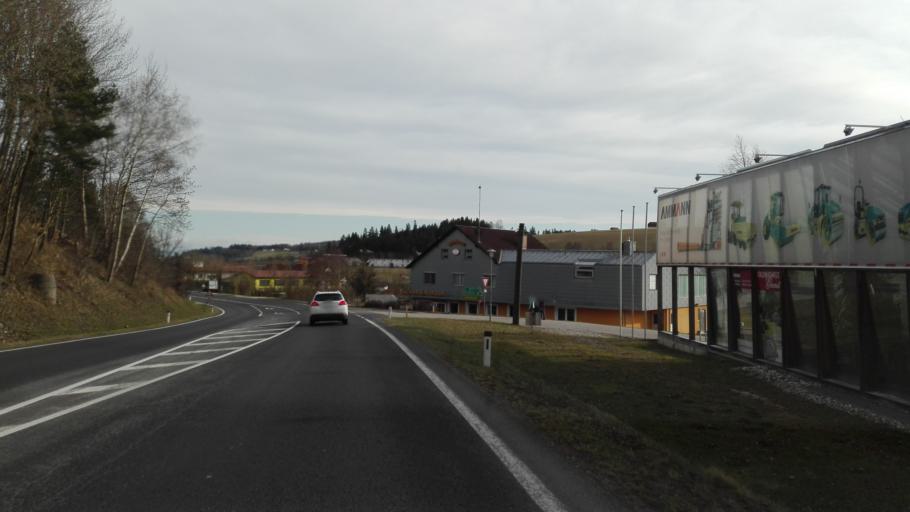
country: AT
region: Upper Austria
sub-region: Politischer Bezirk Urfahr-Umgebung
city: Herzogsdorf
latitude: 48.3992
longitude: 14.0748
